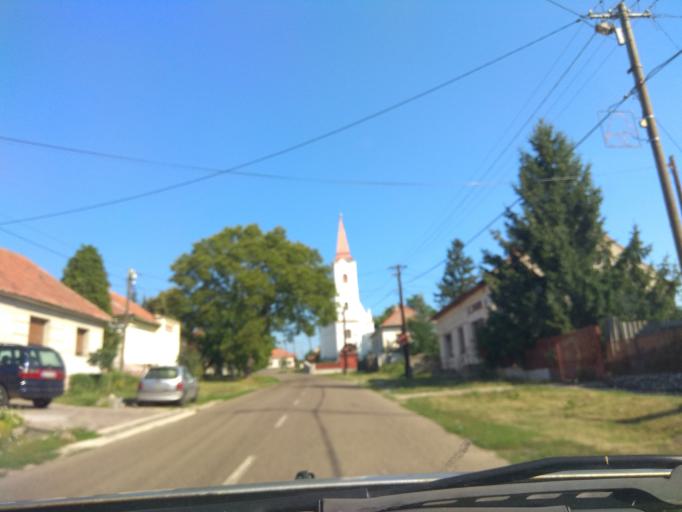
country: HU
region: Borsod-Abauj-Zemplen
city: Emod
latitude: 47.9436
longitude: 20.8140
